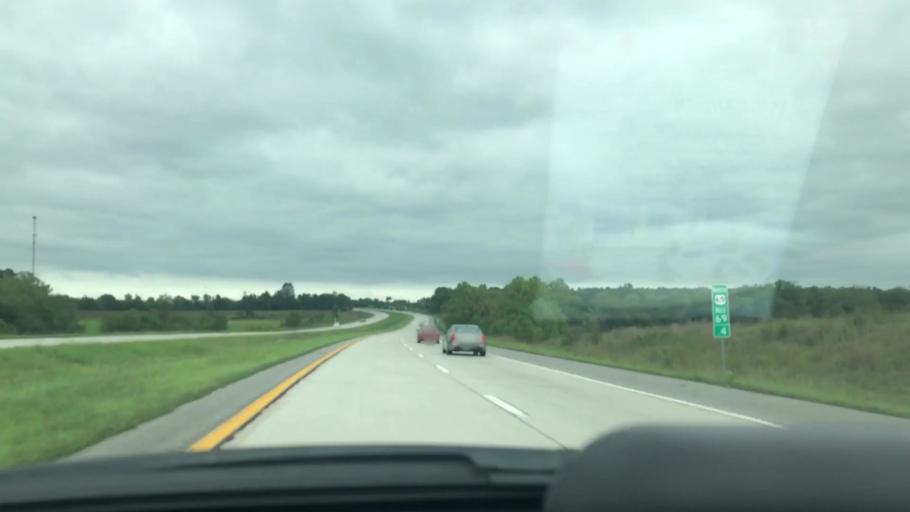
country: US
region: Missouri
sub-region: Greene County
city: Fair Grove
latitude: 37.4485
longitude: -93.1432
